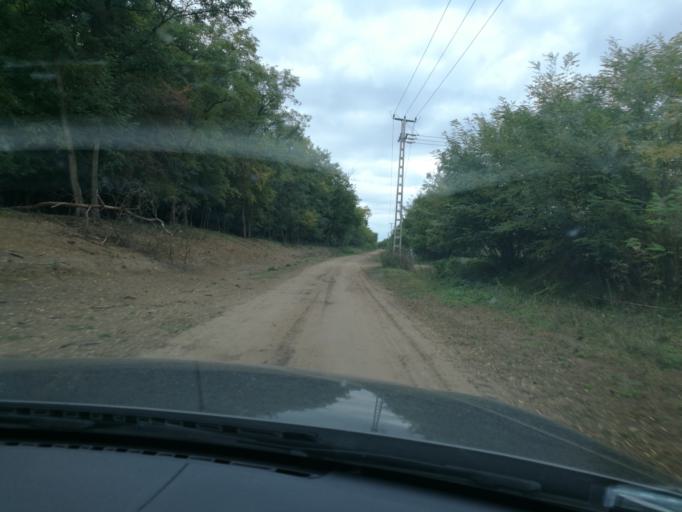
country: HU
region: Szabolcs-Szatmar-Bereg
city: Nyirpazony
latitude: 47.9968
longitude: 21.7883
